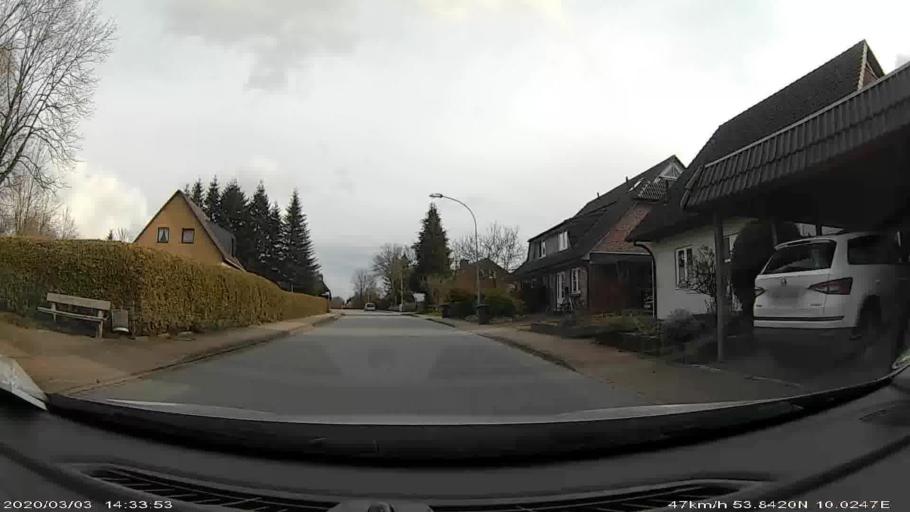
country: DE
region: Schleswig-Holstein
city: Kattendorf
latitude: 53.8420
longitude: 10.0250
